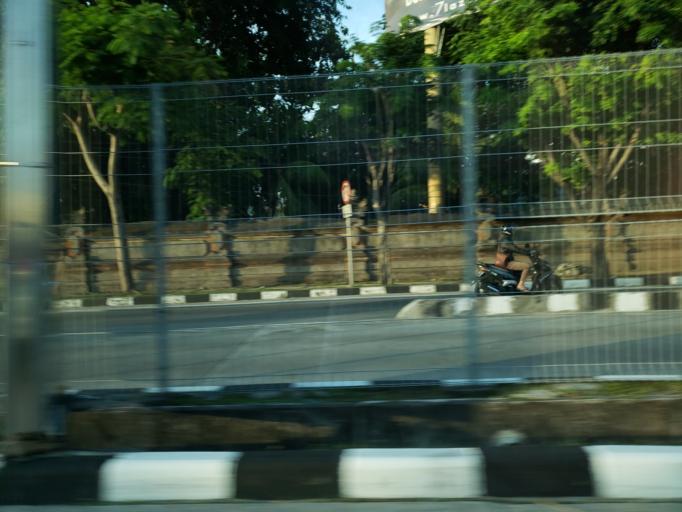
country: ID
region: Bali
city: Kelanabian
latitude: -8.7407
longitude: 115.1678
